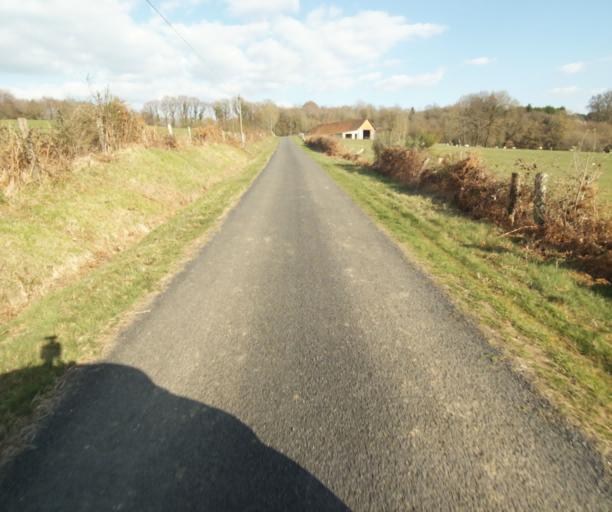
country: FR
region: Limousin
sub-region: Departement de la Correze
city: Saint-Clement
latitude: 45.3448
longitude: 1.6496
